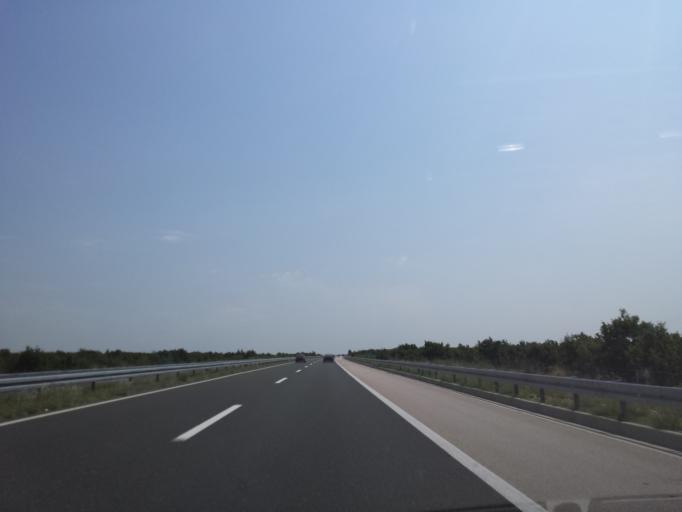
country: HR
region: Zadarska
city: Benkovac
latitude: 43.9850
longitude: 15.6311
